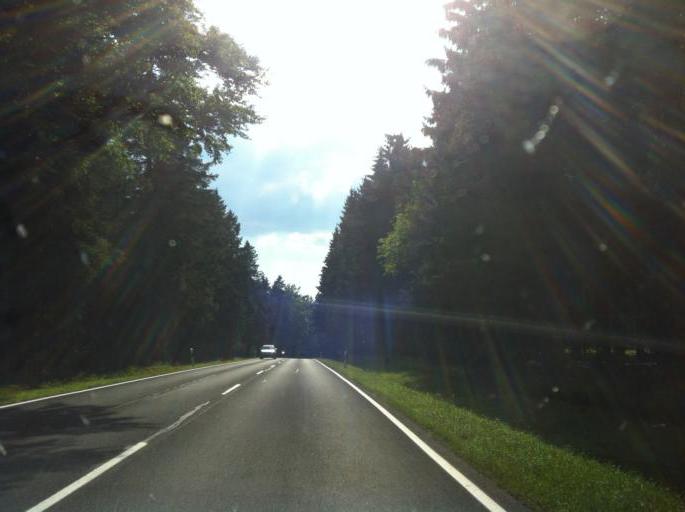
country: DE
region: Thuringia
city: Neuhaus am Rennweg
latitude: 50.4997
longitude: 11.1148
